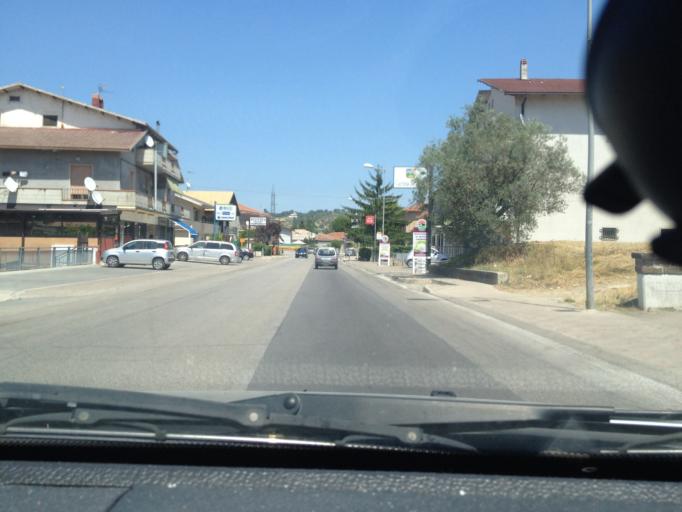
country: IT
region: Abruzzo
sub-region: Provincia di Pescara
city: Cappelle sul Tavo
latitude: 42.4755
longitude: 14.1078
